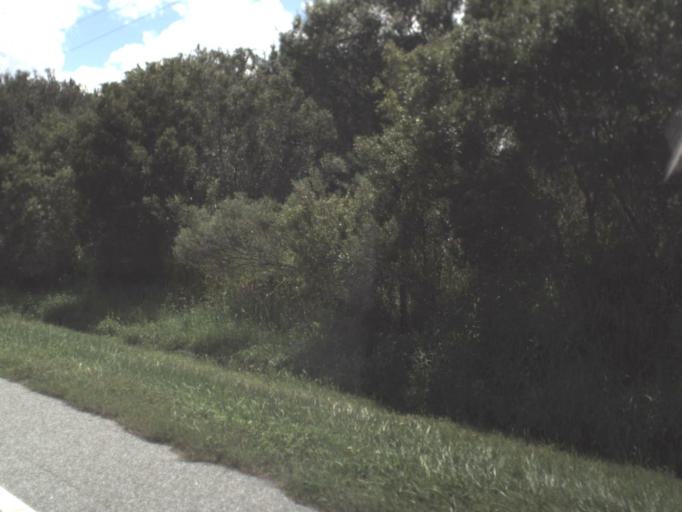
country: US
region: Florida
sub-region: DeSoto County
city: Arcadia
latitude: 27.3167
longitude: -82.1121
